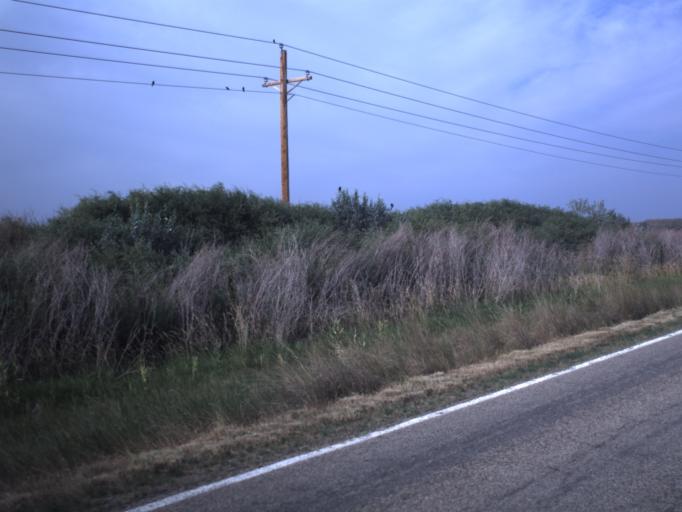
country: US
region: Utah
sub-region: Duchesne County
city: Roosevelt
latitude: 40.2580
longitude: -110.1660
